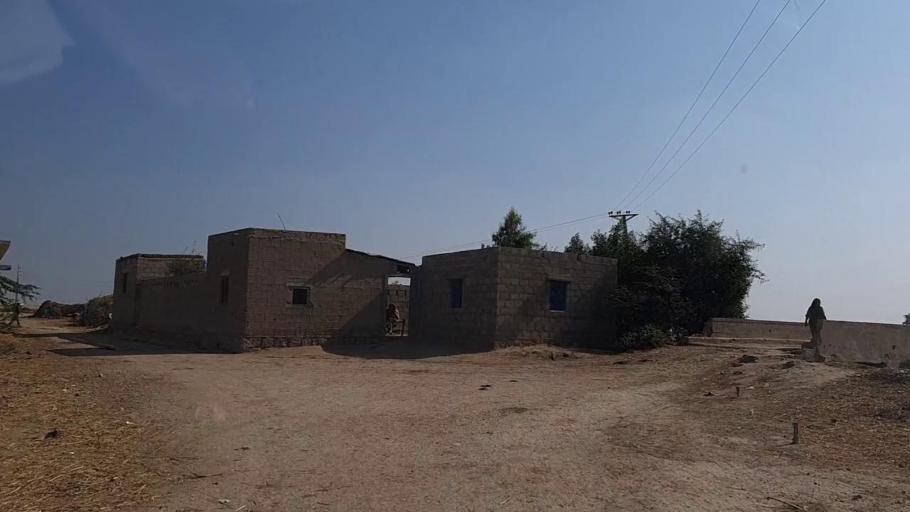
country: PK
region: Sindh
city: Thatta
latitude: 24.7627
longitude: 67.9465
